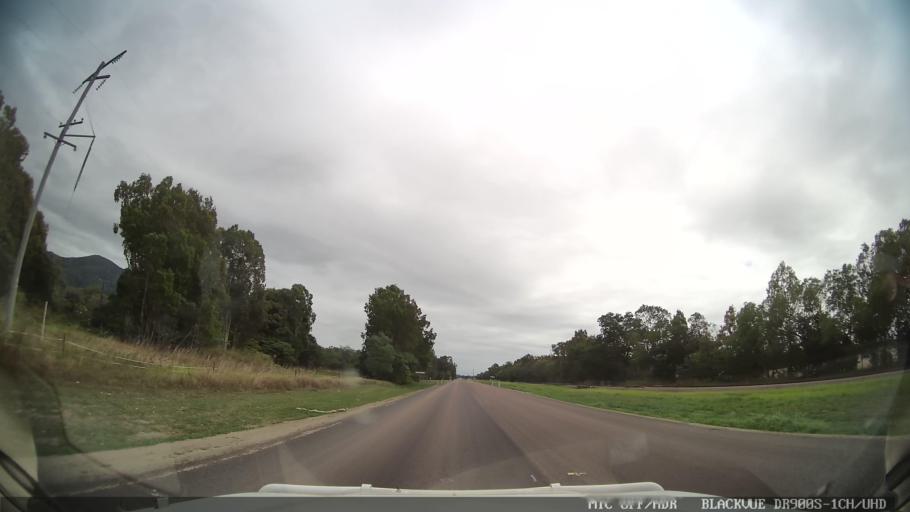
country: AU
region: Queensland
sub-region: Hinchinbrook
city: Ingham
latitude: -18.9324
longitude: 146.2681
